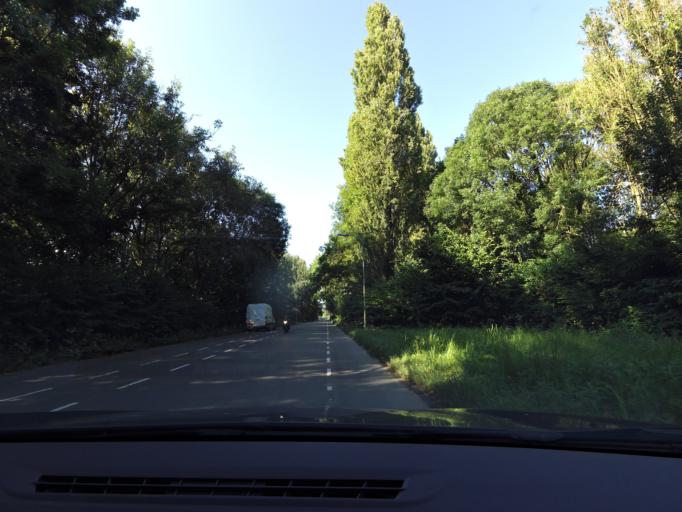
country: NL
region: South Holland
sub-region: Gemeente Dordrecht
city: Dordrecht
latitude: 51.7796
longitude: 4.6883
